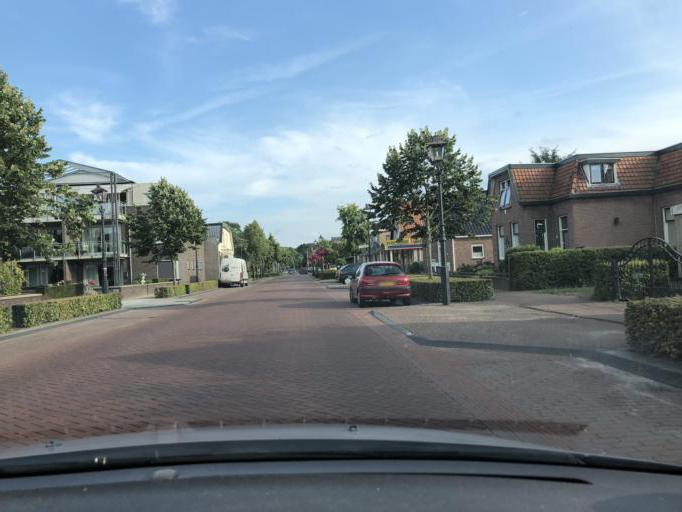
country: NL
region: Overijssel
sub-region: Gemeente Dalfsen
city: Dalfsen
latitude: 52.5763
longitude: 6.2907
